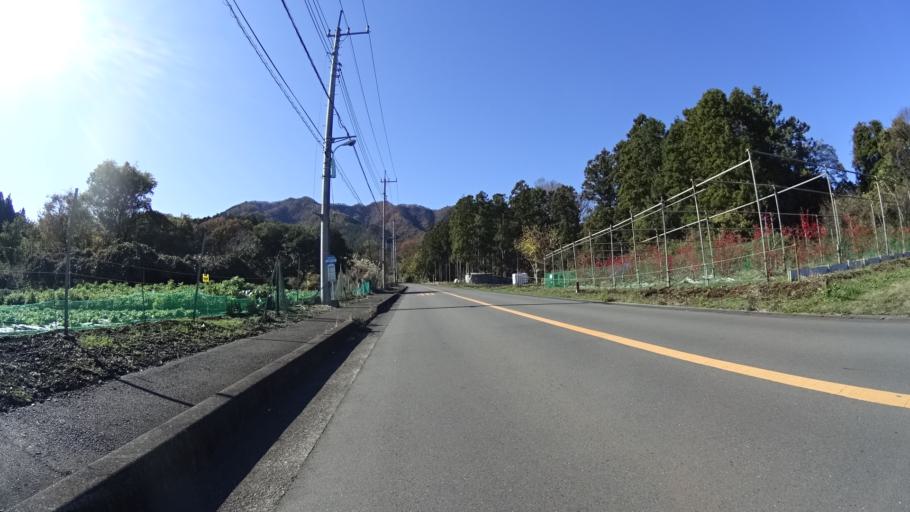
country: JP
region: Kanagawa
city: Zama
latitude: 35.5298
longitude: 139.2778
